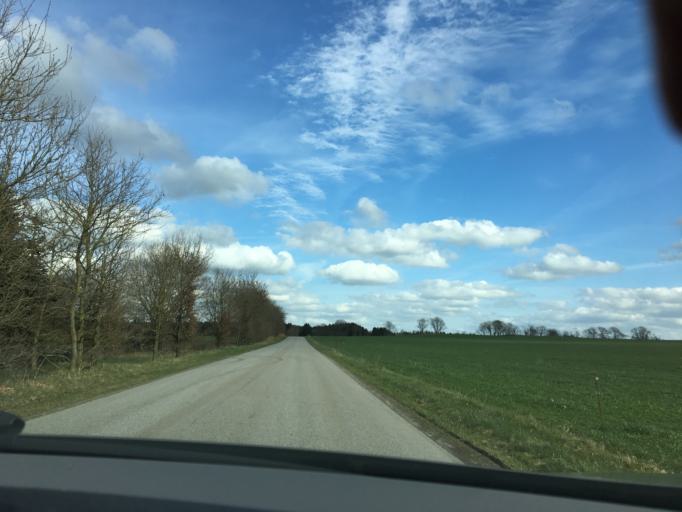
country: DK
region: South Denmark
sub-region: Vejle Kommune
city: Give
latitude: 55.8252
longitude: 9.2999
